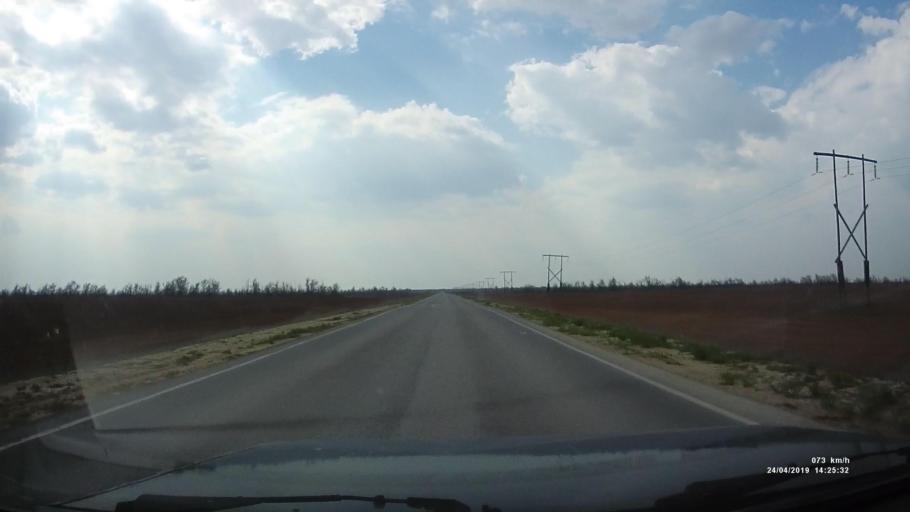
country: RU
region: Kalmykiya
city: Arshan'
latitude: 46.3316
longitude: 44.0798
